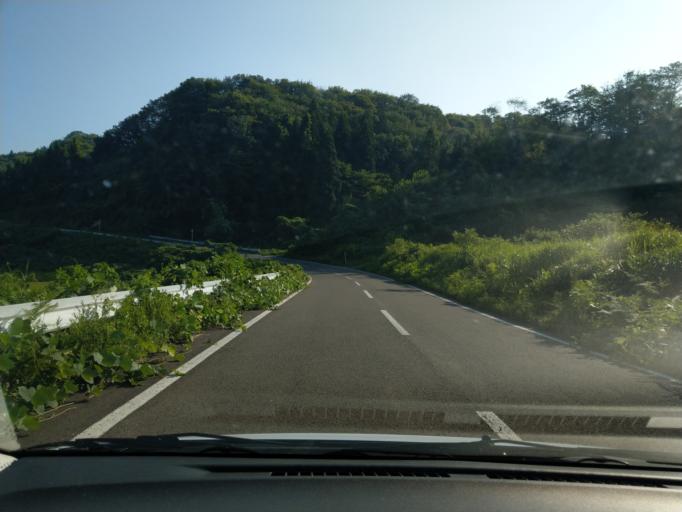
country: JP
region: Akita
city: Akita
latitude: 39.5828
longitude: 140.2347
